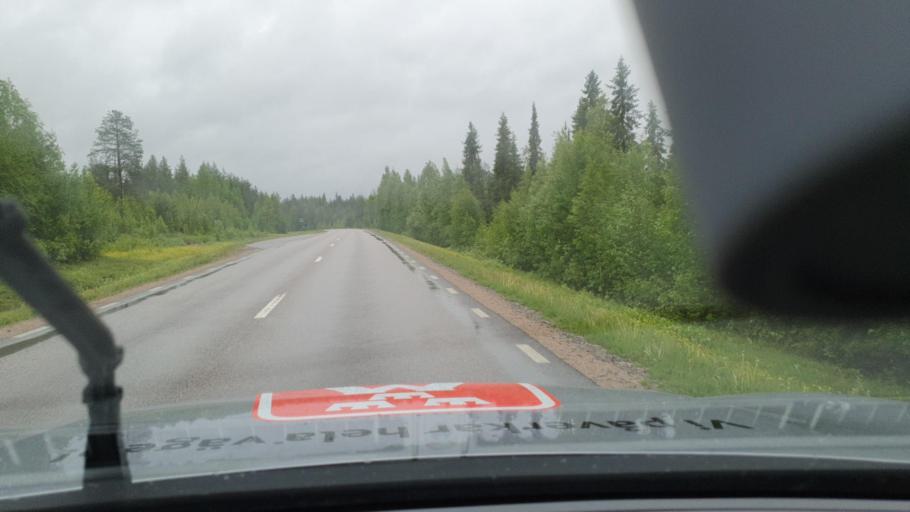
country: SE
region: Norrbotten
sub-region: Overtornea Kommun
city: OEvertornea
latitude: 66.4099
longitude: 23.4482
